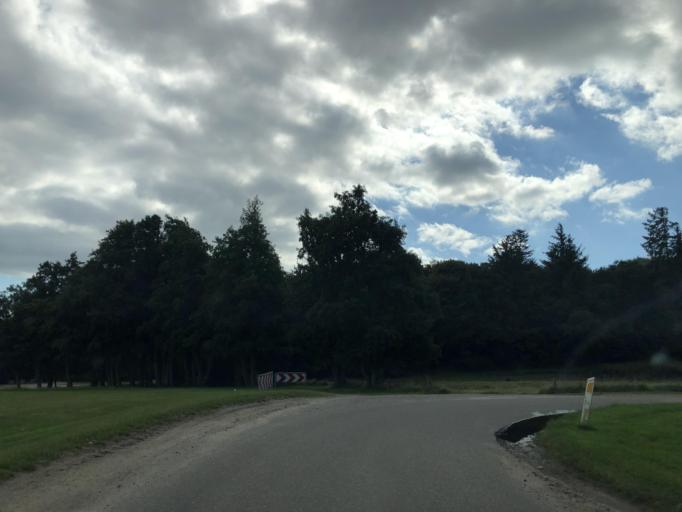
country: DK
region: Central Jutland
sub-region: Viborg Kommune
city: Viborg
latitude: 56.5661
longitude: 9.3226
